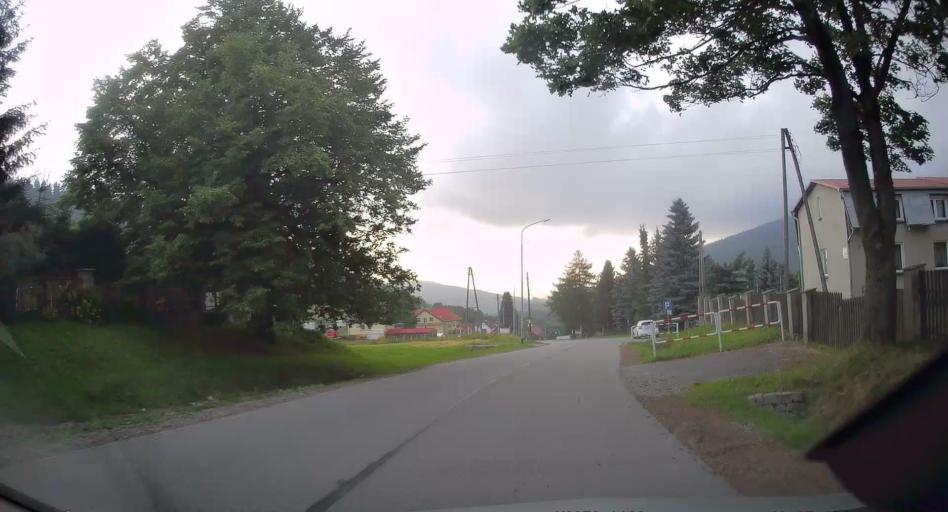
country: PL
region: Lower Silesian Voivodeship
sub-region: Powiat klodzki
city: Ludwikowice Klodzkie
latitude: 50.6631
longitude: 16.4644
